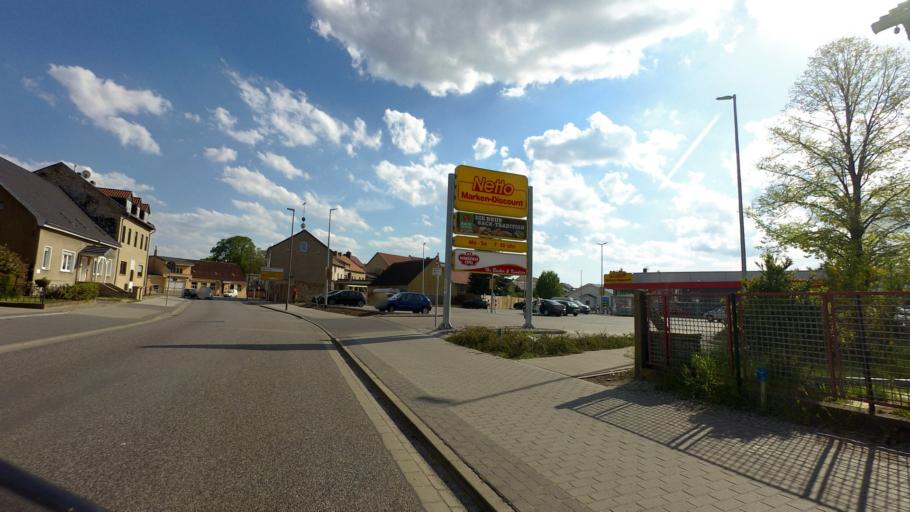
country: DE
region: Brandenburg
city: Zehdenick
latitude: 52.9860
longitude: 13.3402
